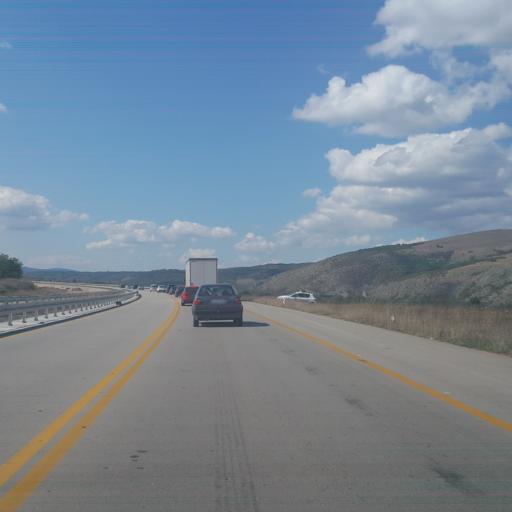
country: RS
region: Central Serbia
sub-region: Pirotski Okrug
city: Bela Palanka
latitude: 43.2235
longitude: 22.4040
